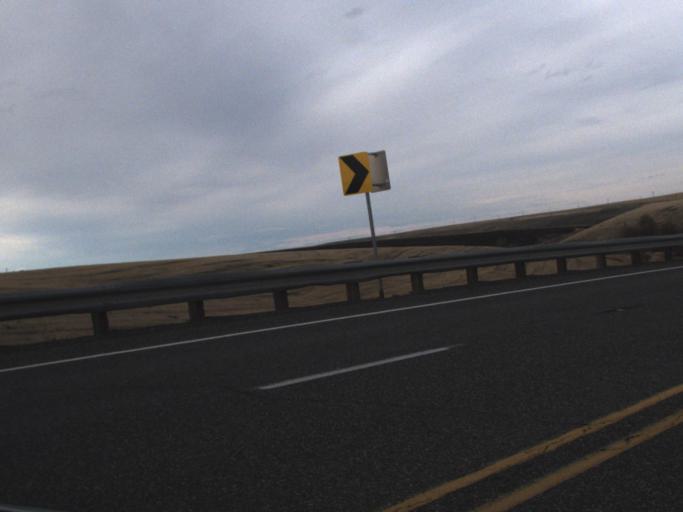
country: US
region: Washington
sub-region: Garfield County
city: Pomeroy
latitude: 46.4375
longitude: -117.4324
